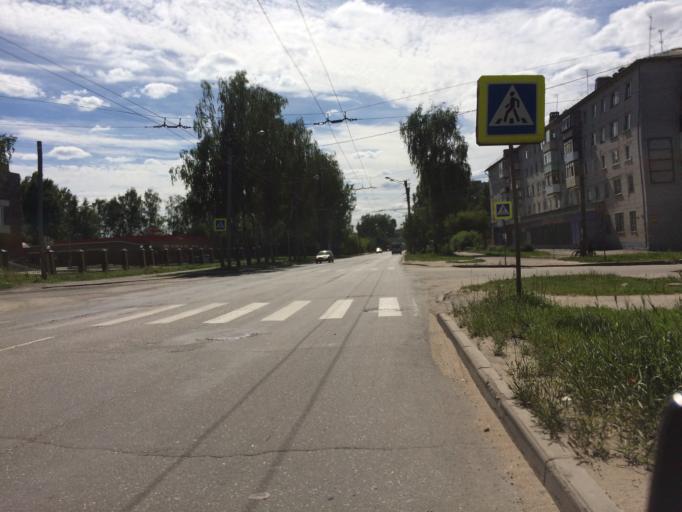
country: RU
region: Mariy-El
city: Yoshkar-Ola
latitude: 56.6388
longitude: 47.9500
